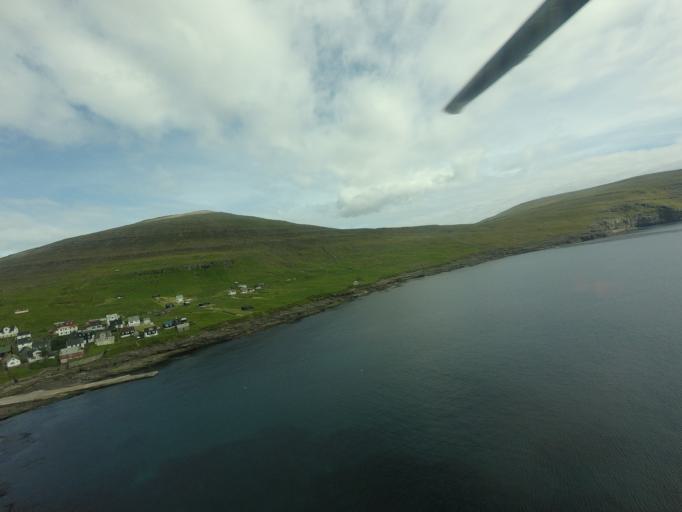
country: FO
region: Nordoyar
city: Klaksvik
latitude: 62.2760
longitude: -6.3381
